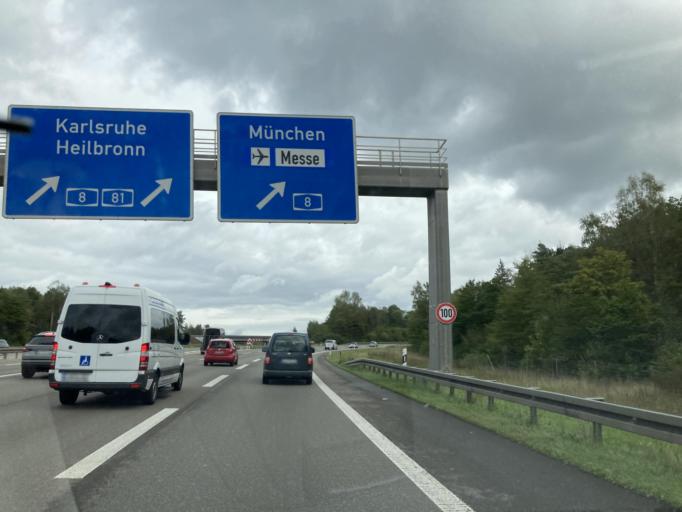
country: DE
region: Baden-Wuerttemberg
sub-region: Regierungsbezirk Stuttgart
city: Sindelfingen
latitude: 48.7236
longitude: 9.0638
